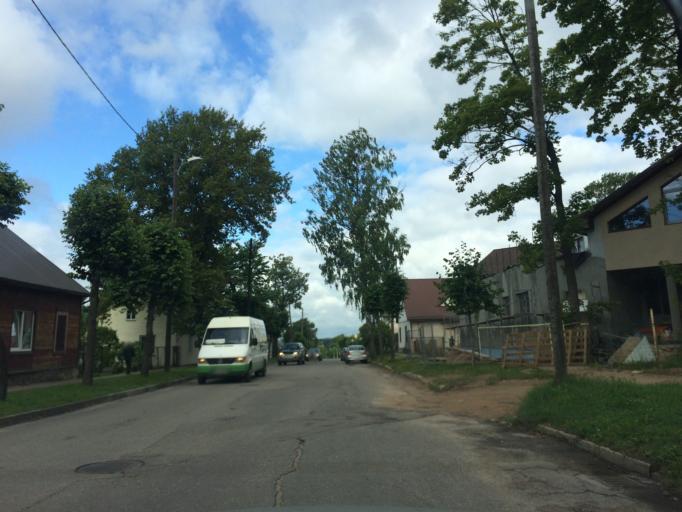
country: LV
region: Rezekne
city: Rezekne
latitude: 56.5087
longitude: 27.3304
